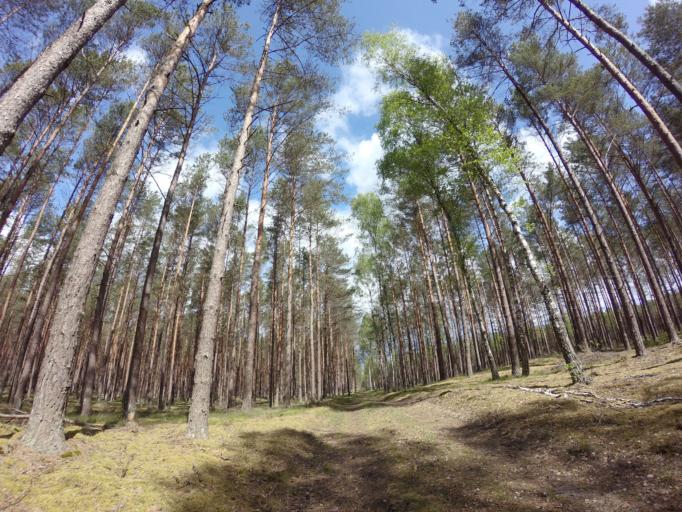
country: PL
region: West Pomeranian Voivodeship
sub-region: Powiat drawski
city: Kalisz Pomorski
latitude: 53.1970
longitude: 15.9846
